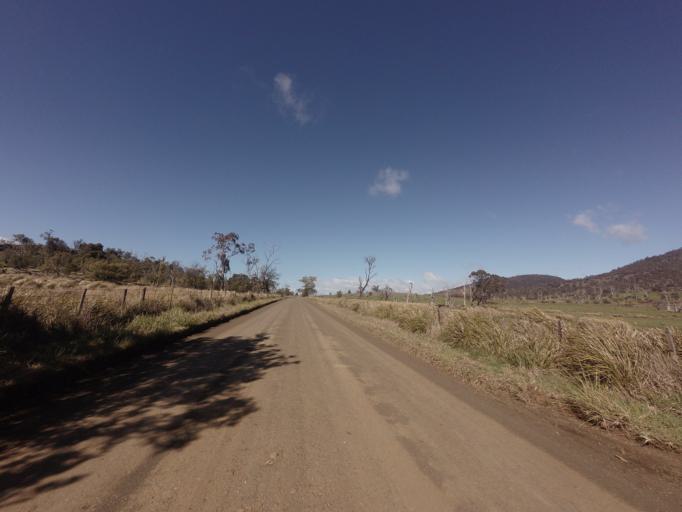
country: AU
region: Tasmania
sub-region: Northern Midlands
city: Evandale
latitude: -41.9362
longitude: 147.4200
